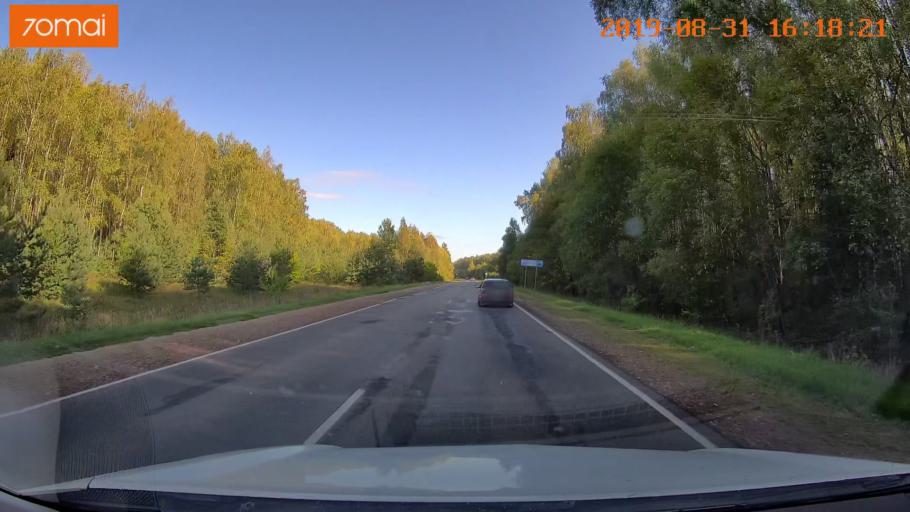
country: RU
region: Kaluga
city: Nikola-Lenivets
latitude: 54.5372
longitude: 35.5533
